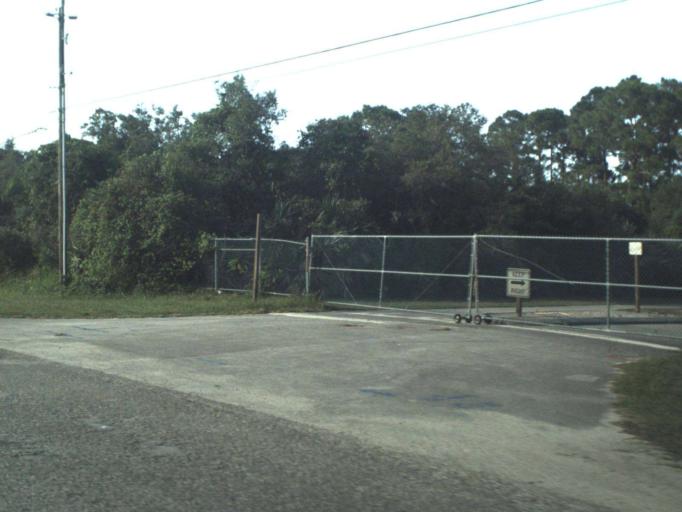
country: US
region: Florida
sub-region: Volusia County
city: Oak Hill
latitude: 28.9252
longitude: -80.8740
